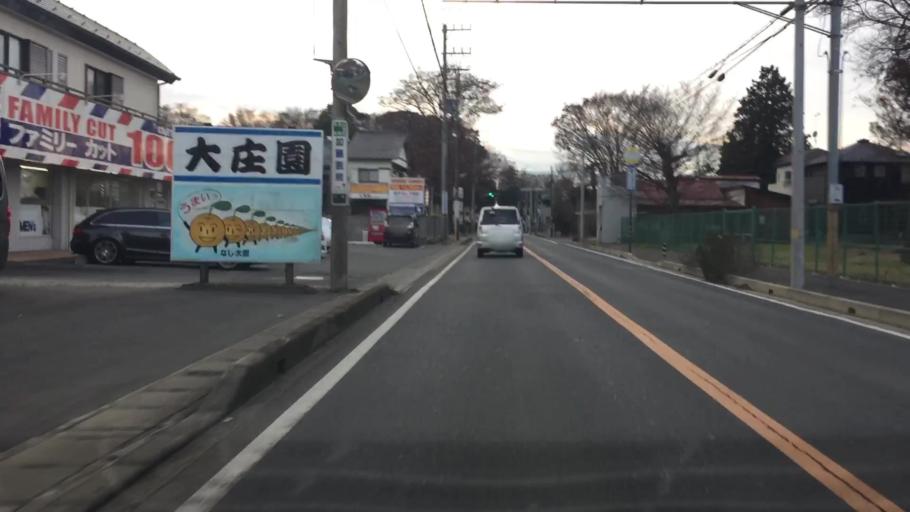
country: JP
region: Chiba
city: Matsudo
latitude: 35.7687
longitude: 139.9612
